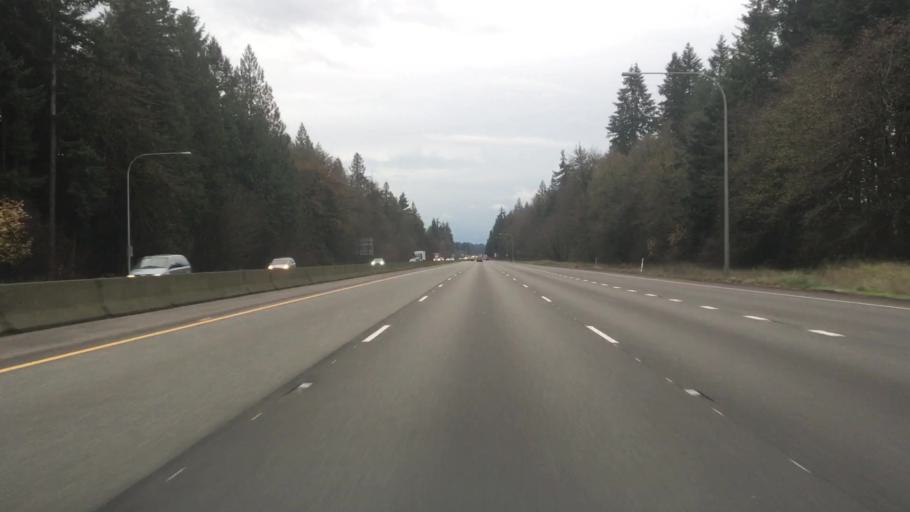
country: US
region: Washington
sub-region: Thurston County
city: Tumwater
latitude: 46.9488
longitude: -122.9388
